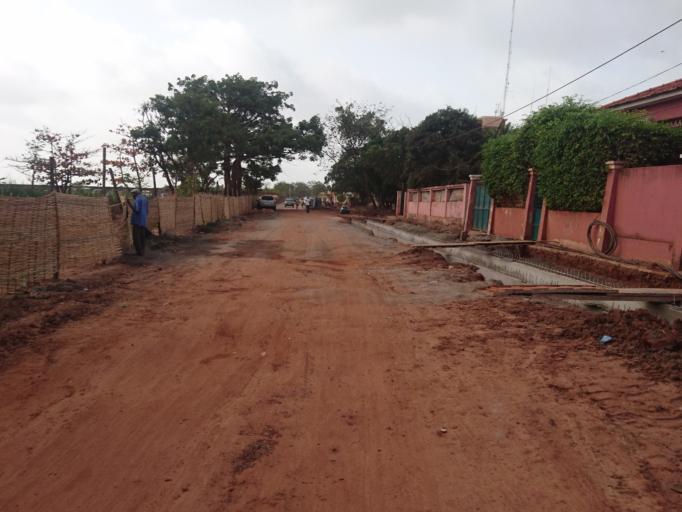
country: GW
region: Bissau
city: Bissau
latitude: 11.8567
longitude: -15.5851
